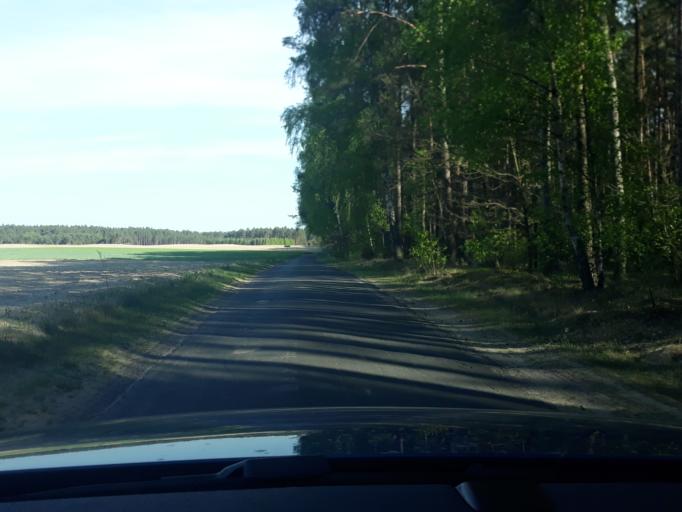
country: PL
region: Pomeranian Voivodeship
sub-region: Powiat czluchowski
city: Przechlewo
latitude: 53.8651
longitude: 17.3369
